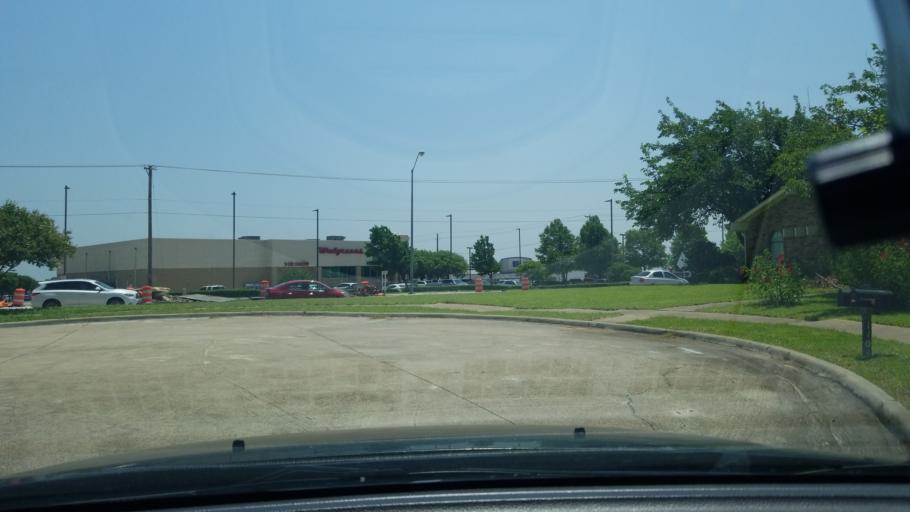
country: US
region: Texas
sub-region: Dallas County
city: Mesquite
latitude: 32.8121
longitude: -96.6117
